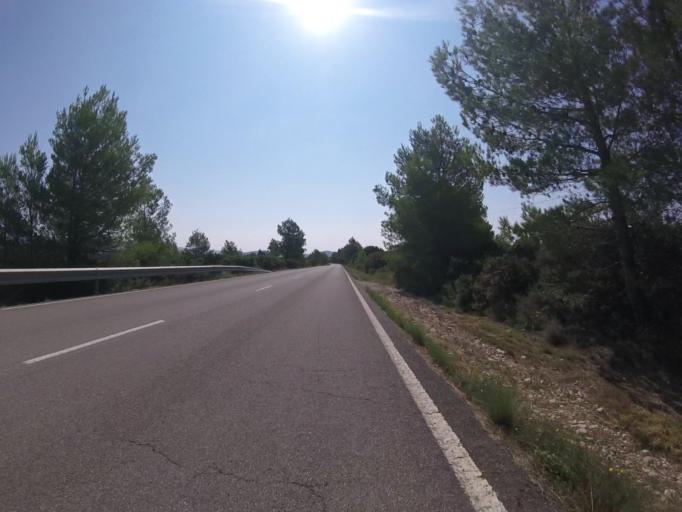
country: ES
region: Valencia
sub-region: Provincia de Castello
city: Benafigos
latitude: 40.2453
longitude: -0.1960
